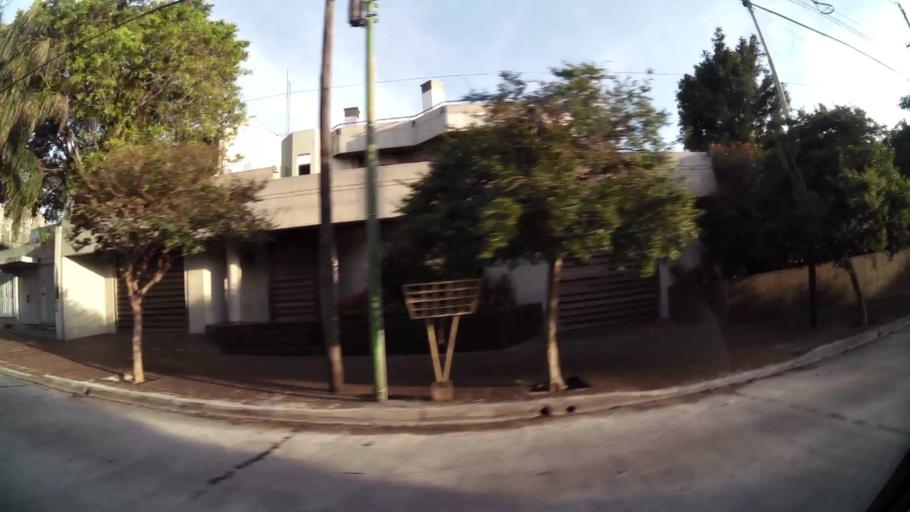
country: AR
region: Buenos Aires F.D.
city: Villa Santa Rita
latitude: -34.6378
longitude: -58.4481
